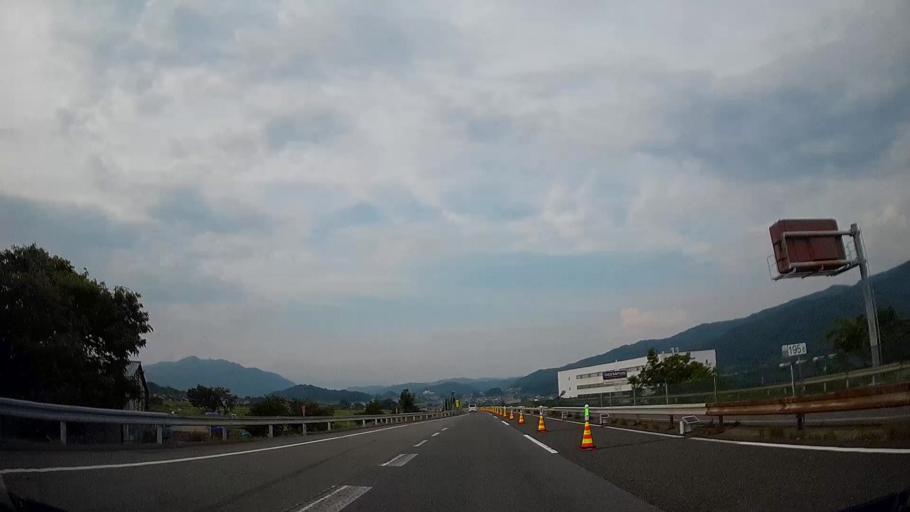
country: JP
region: Nagano
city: Tatsuno
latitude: 35.9467
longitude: 137.9846
